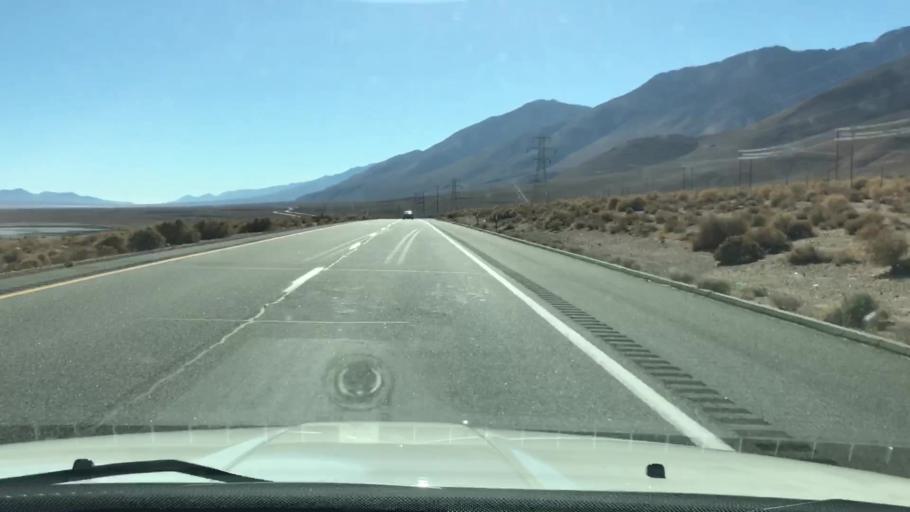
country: US
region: California
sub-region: Inyo County
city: Lone Pine
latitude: 36.4775
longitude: -118.0359
